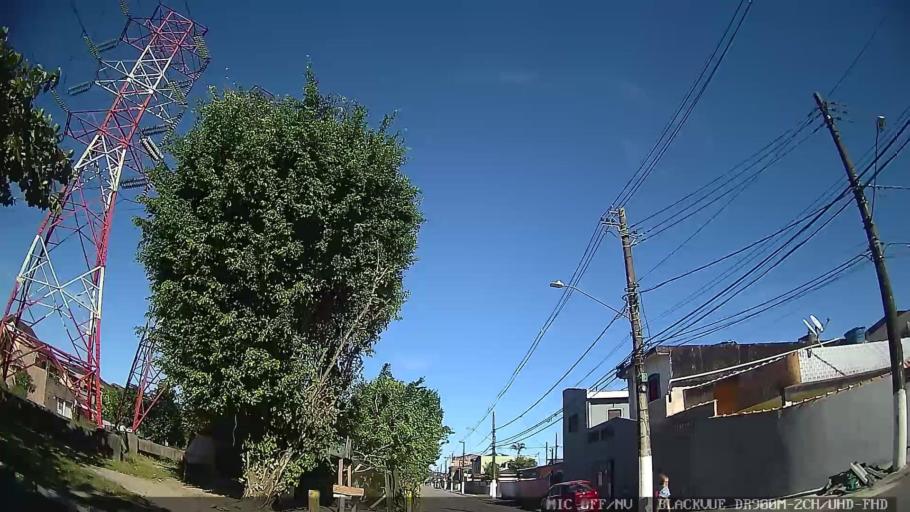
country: BR
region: Sao Paulo
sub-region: Santos
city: Santos
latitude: -23.9353
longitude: -46.2872
